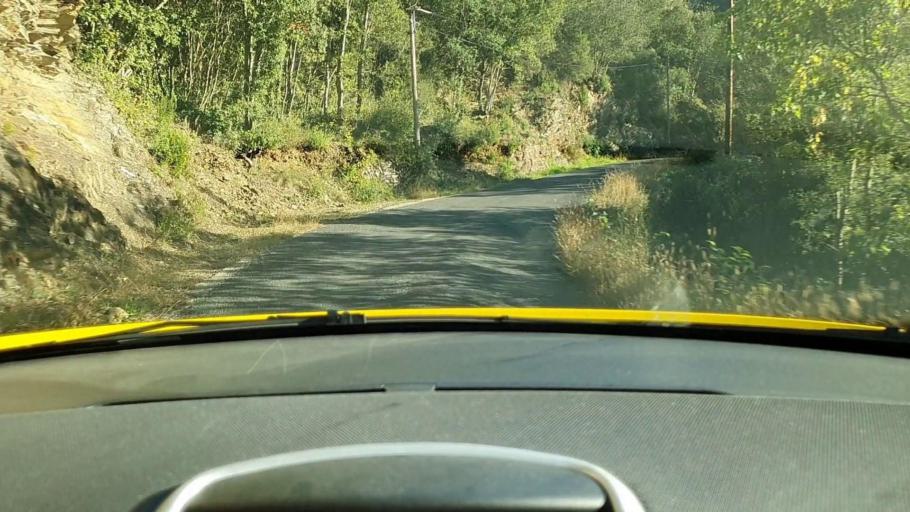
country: FR
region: Languedoc-Roussillon
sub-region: Departement du Gard
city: Sumene
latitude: 44.0198
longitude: 3.7348
